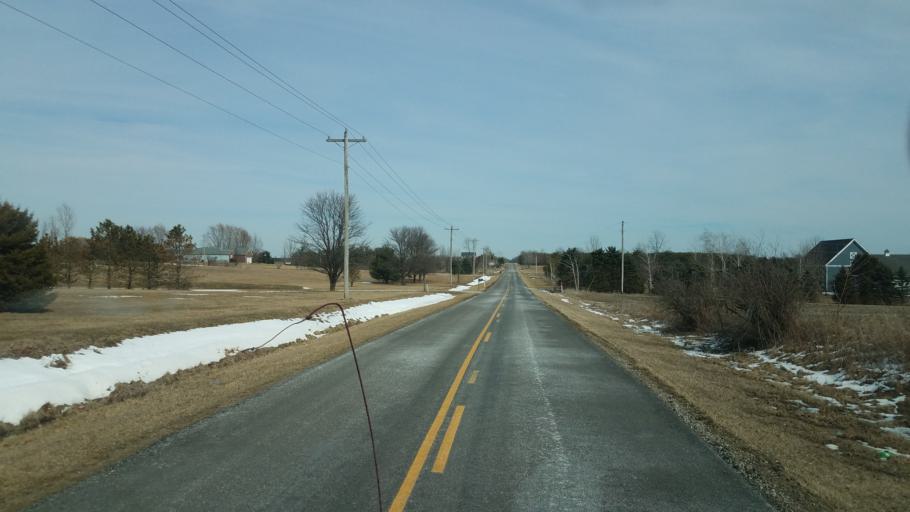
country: US
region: Ohio
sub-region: Delaware County
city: Ashley
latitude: 40.3391
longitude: -82.9847
